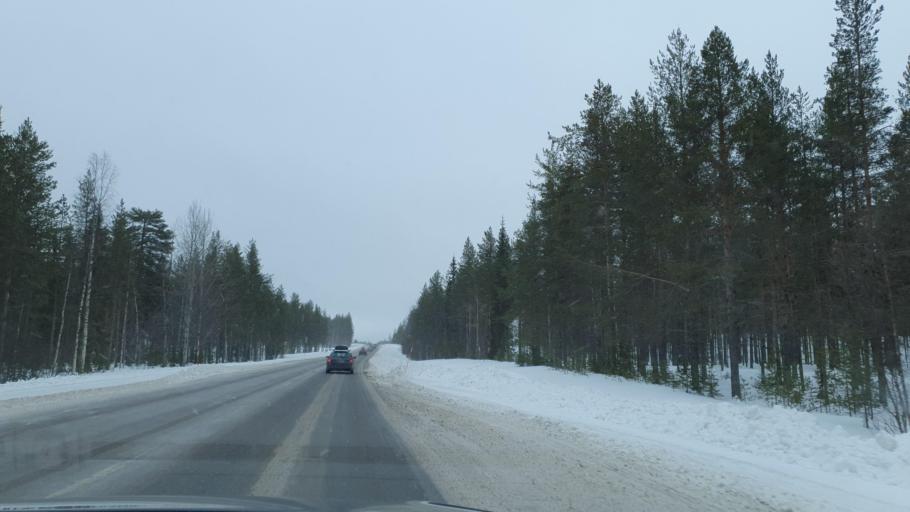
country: FI
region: Lapland
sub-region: Torniolaakso
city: Pello
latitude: 66.9363
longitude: 24.0793
